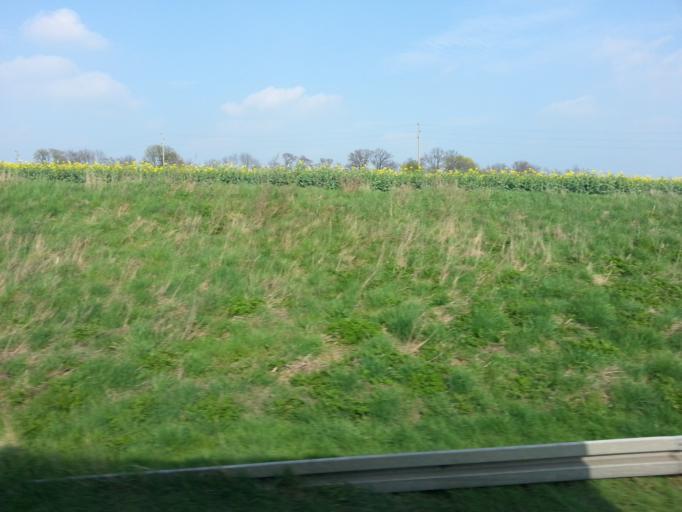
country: DE
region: Brandenburg
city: Fehrbellin
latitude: 52.8536
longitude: 12.7736
